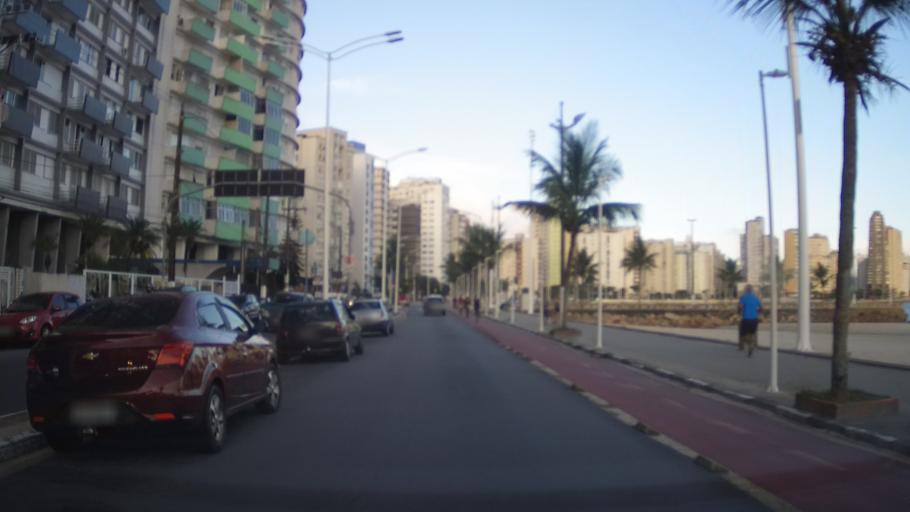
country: BR
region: Sao Paulo
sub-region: Sao Vicente
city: Sao Vicente
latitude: -23.9690
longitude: -46.3796
